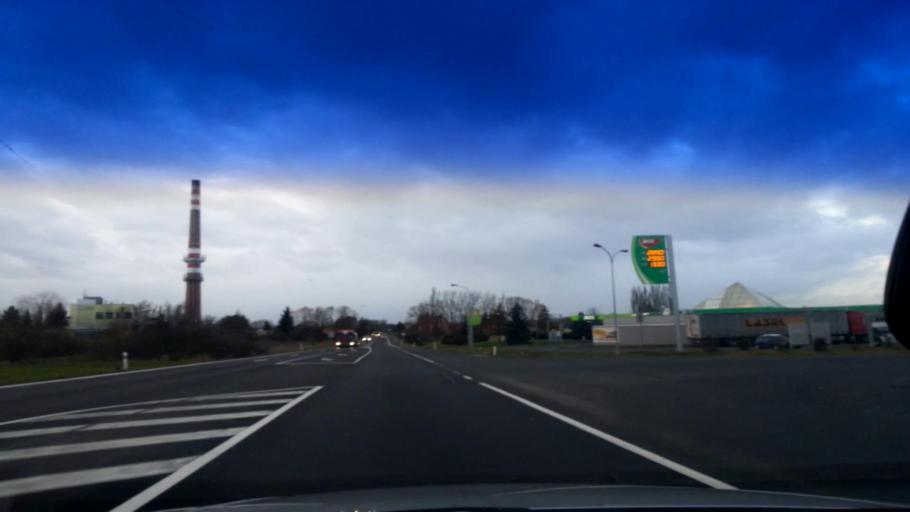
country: CZ
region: Karlovarsky
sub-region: Okres Cheb
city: Frantiskovy Lazne
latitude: 50.1264
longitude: 12.3593
